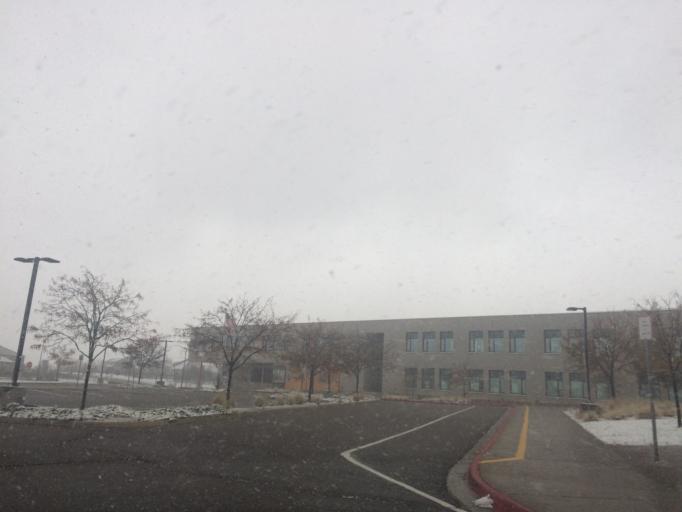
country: US
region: Colorado
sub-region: Boulder County
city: Erie
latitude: 40.0443
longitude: -105.0660
